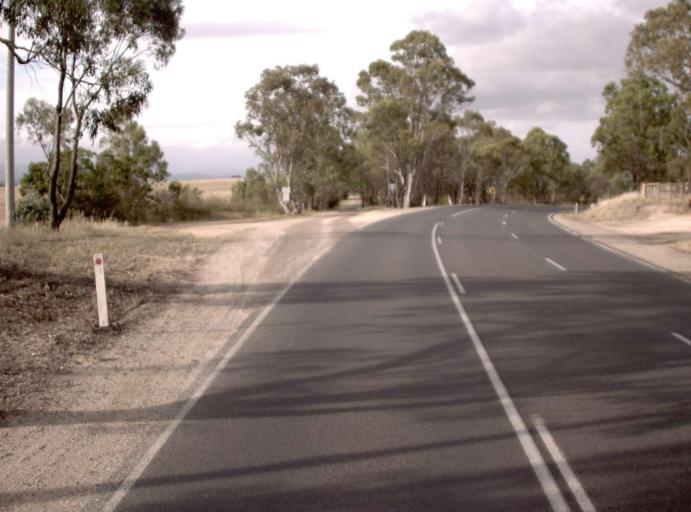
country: AU
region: Victoria
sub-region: Wellington
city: Sale
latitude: -37.9280
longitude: 146.9922
